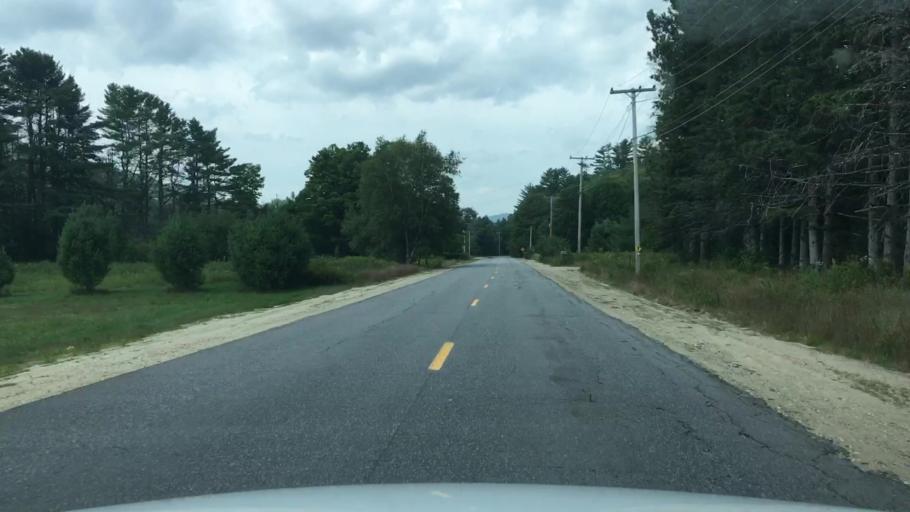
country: US
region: Maine
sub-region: Oxford County
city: Rumford
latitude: 44.5148
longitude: -70.6216
